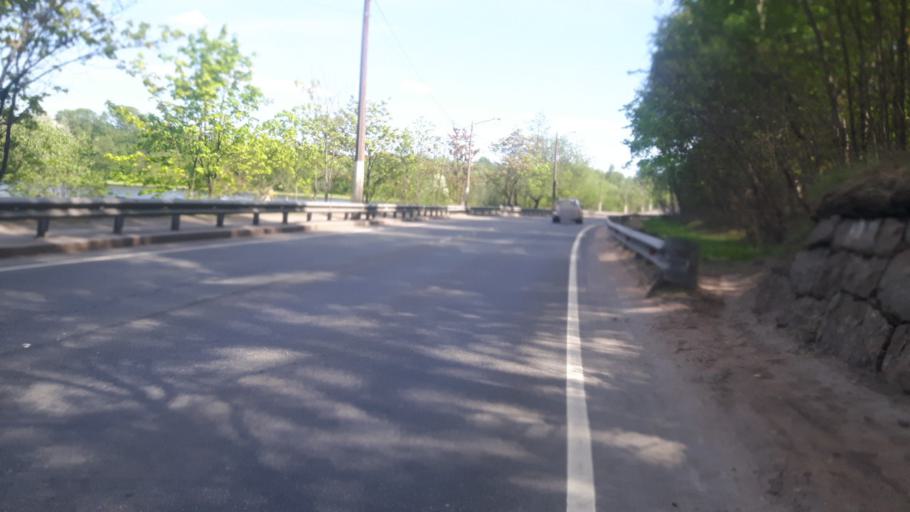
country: RU
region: Leningrad
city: Vyborg
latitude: 60.7241
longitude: 28.7110
